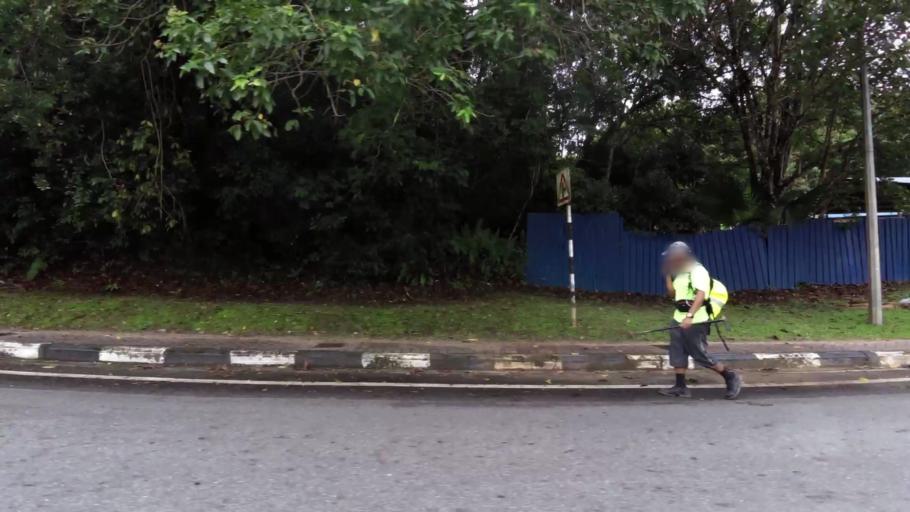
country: BN
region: Brunei and Muara
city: Bandar Seri Begawan
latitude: 4.8991
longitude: 114.9416
